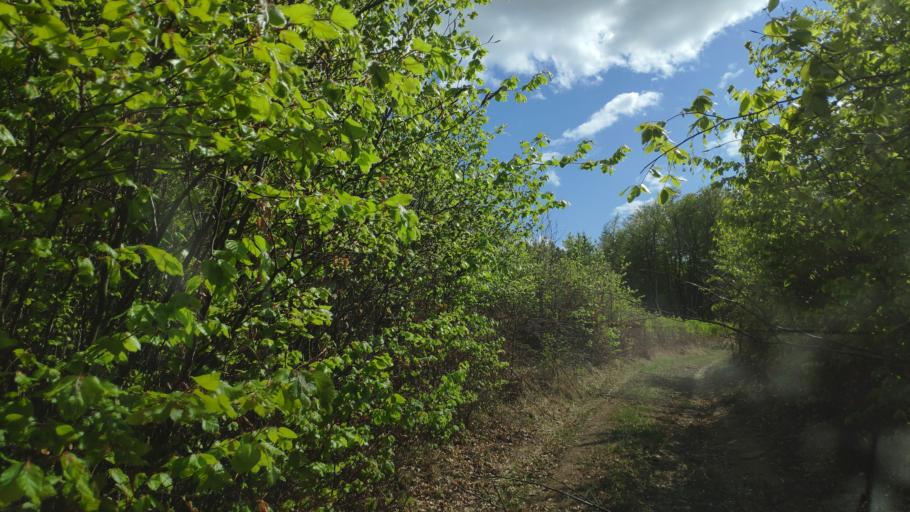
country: SK
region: Kosicky
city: Kosice
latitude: 48.6626
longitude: 21.4503
